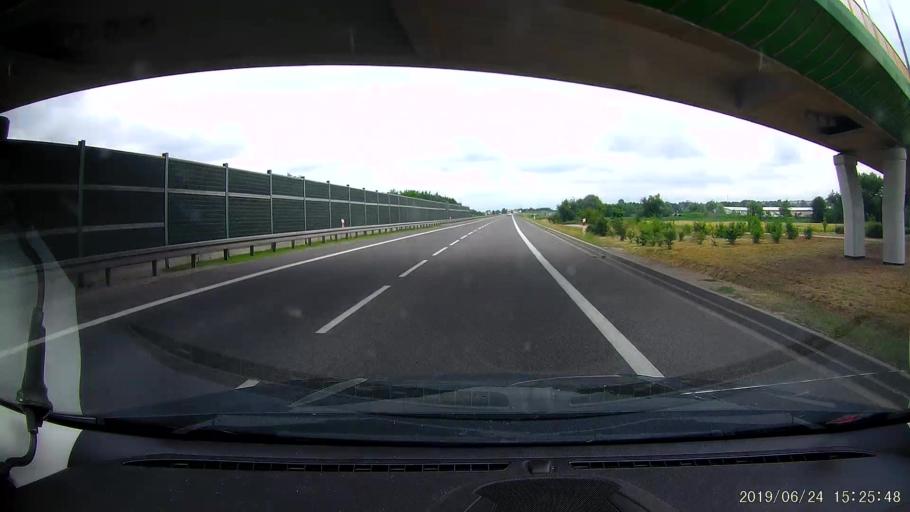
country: PL
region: Subcarpathian Voivodeship
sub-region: Powiat jaroslawski
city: Jaroslaw
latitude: 50.0311
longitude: 22.6843
